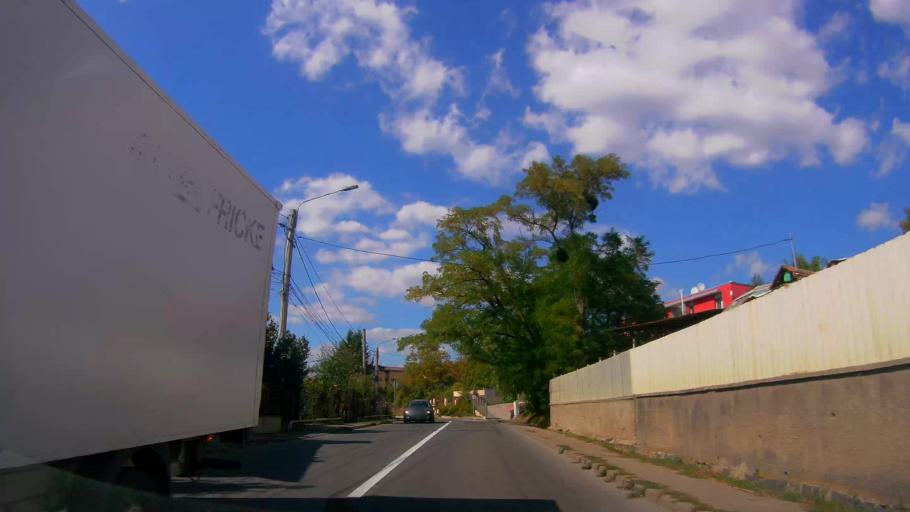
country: RO
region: Salaj
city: Zalau
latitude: 47.1776
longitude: 23.0653
